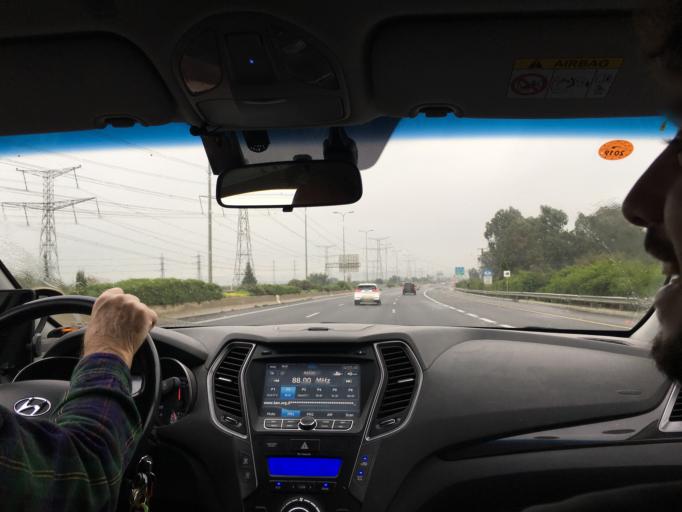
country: IL
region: Central District
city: Petah Tiqwa
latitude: 32.1205
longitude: 34.9101
